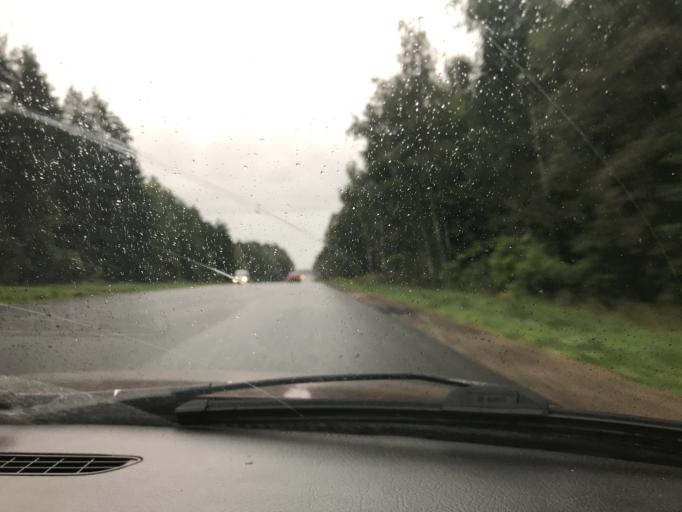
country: RU
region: Kaluga
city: Kurovskoye
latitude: 54.5970
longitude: 36.0556
